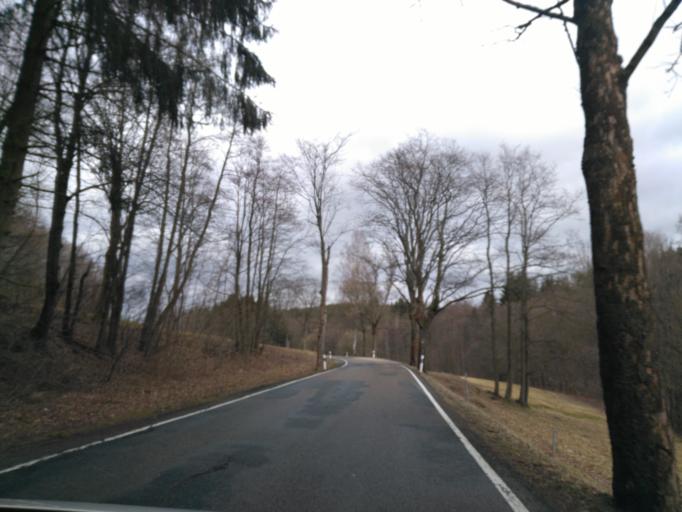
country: DE
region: Saxony
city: Konigswalde
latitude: 50.5760
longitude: 13.0532
